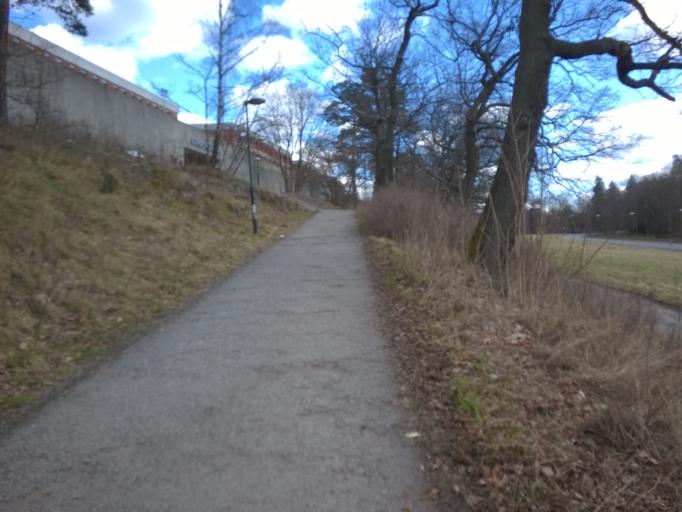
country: SE
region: Stockholm
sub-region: Norrtalje Kommun
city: Bergshamra
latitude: 59.3696
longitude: 18.0618
